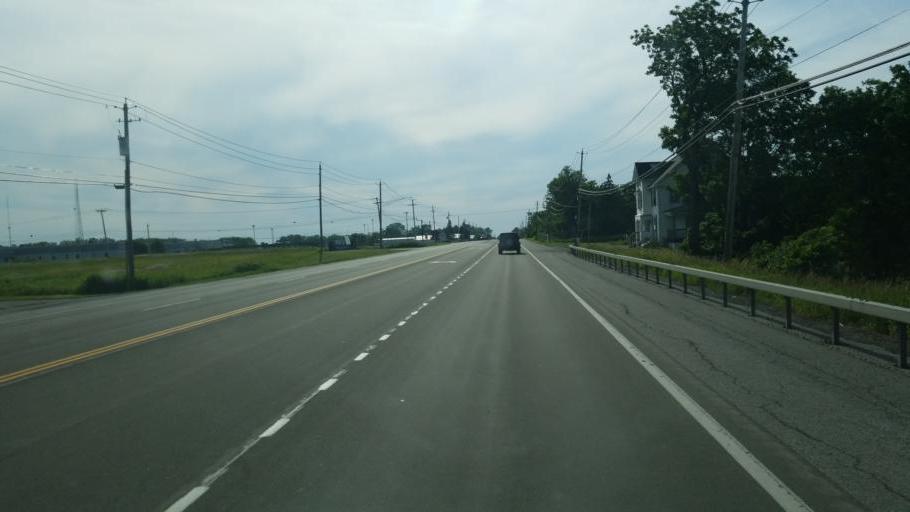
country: US
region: New York
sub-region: Genesee County
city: Batavia
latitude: 42.9908
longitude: -78.1393
